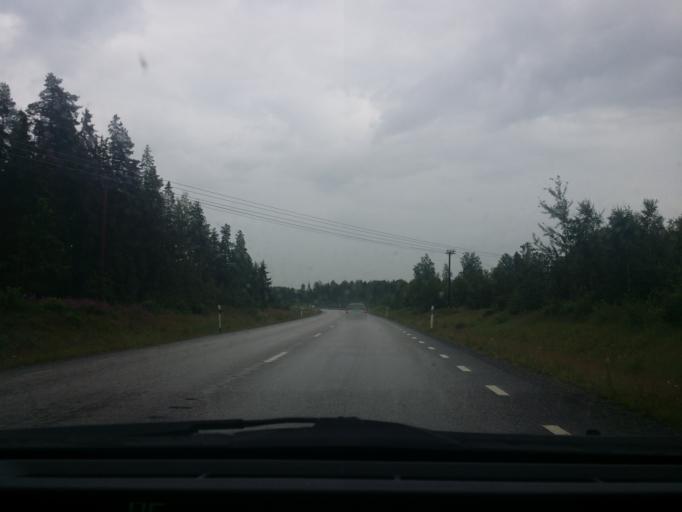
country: SE
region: OErebro
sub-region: Lindesbergs Kommun
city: Frovi
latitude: 59.4602
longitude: 15.4369
